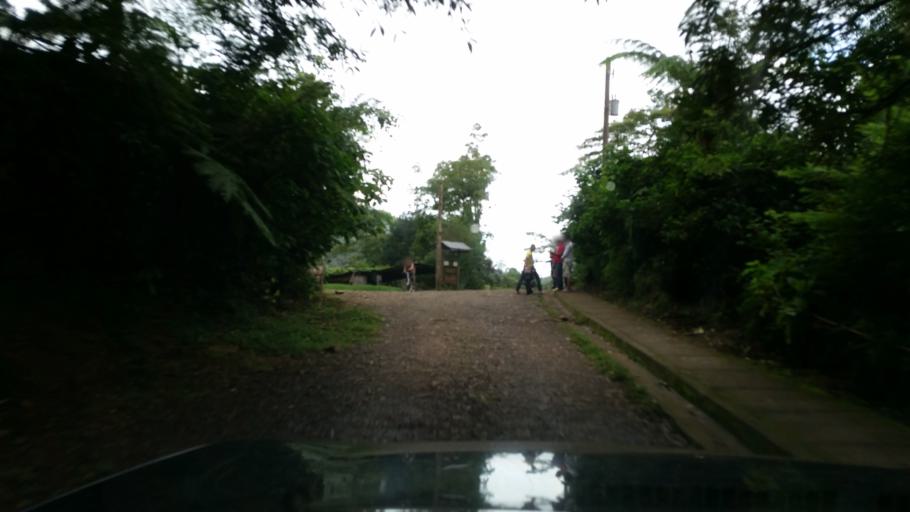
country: NI
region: Jinotega
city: San Jose de Bocay
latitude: 13.2784
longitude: -85.7173
